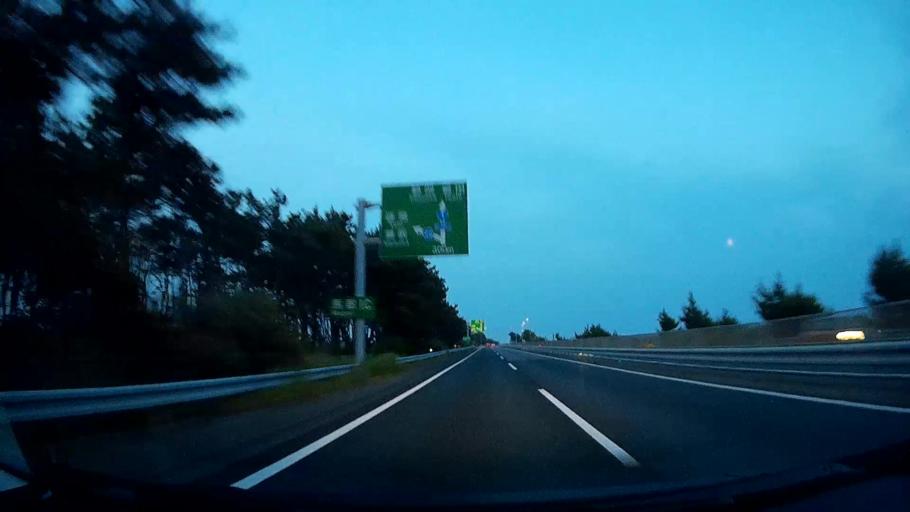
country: JP
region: Shizuoka
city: Kosai-shi
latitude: 34.6775
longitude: 137.6245
